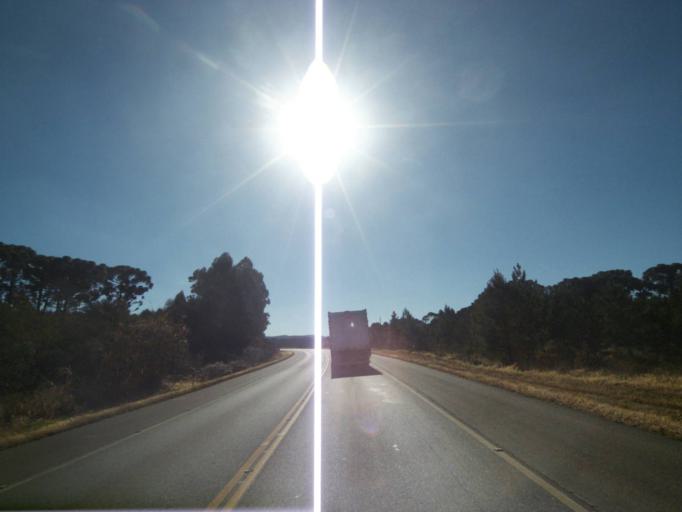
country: BR
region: Parana
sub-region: Tibagi
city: Tibagi
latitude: -24.5835
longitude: -50.4380
